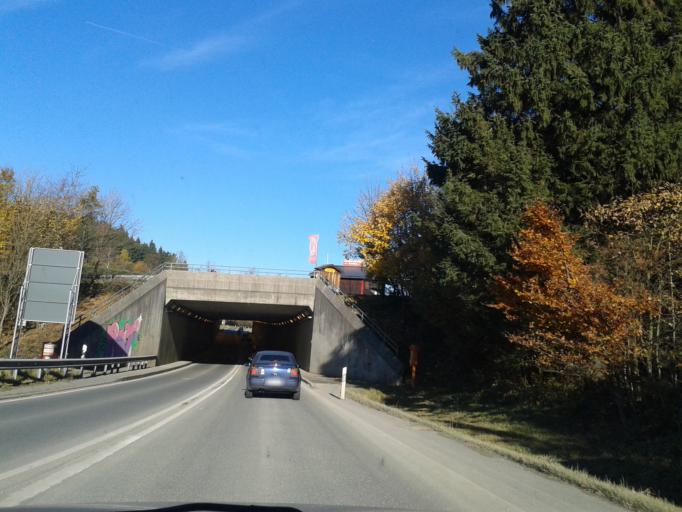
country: DE
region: North Rhine-Westphalia
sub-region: Regierungsbezirk Arnsberg
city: Winterberg
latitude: 51.1921
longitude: 8.5185
